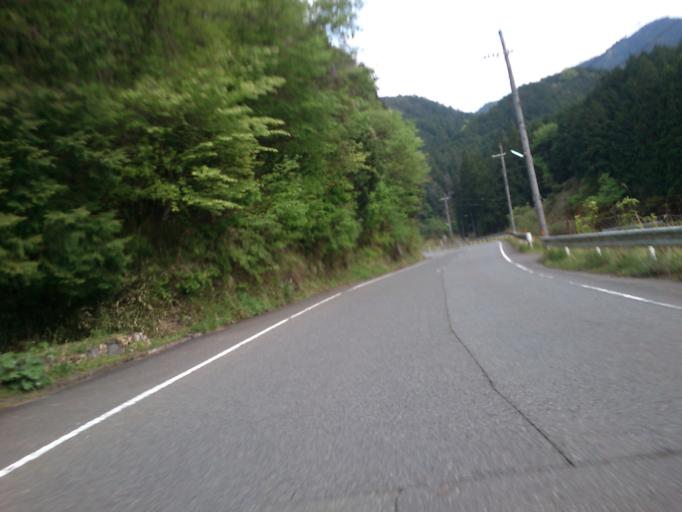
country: JP
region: Kyoto
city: Fukuchiyama
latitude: 35.3067
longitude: 134.9756
